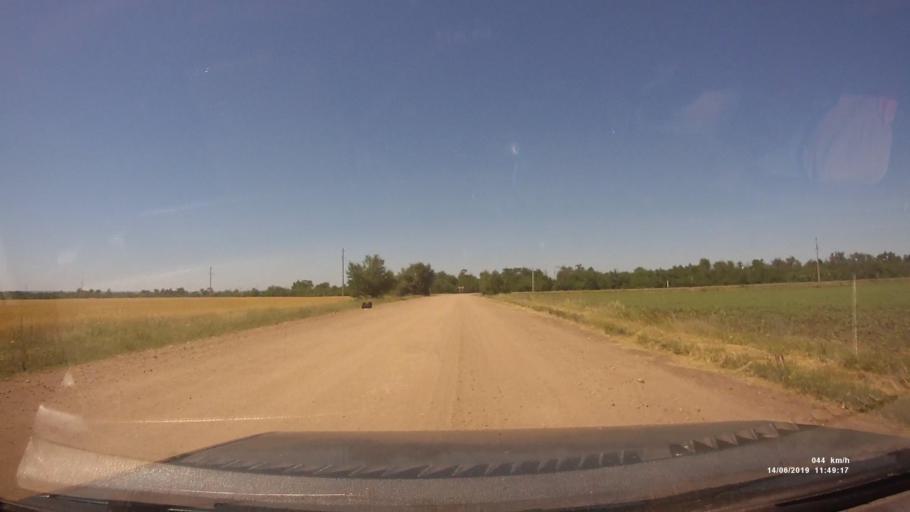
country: RU
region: Rostov
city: Kazanskaya
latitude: 49.8529
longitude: 41.2782
